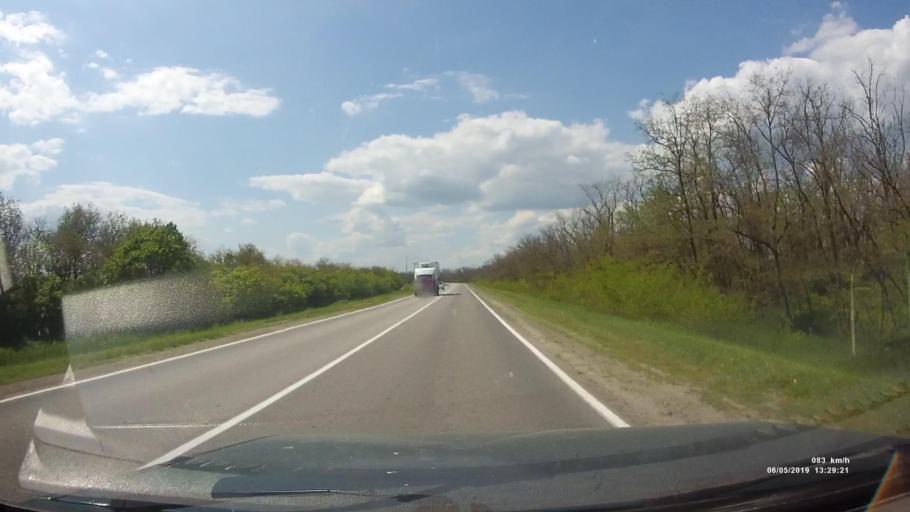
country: RU
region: Rostov
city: Ust'-Donetskiy
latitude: 47.6709
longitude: 40.8460
